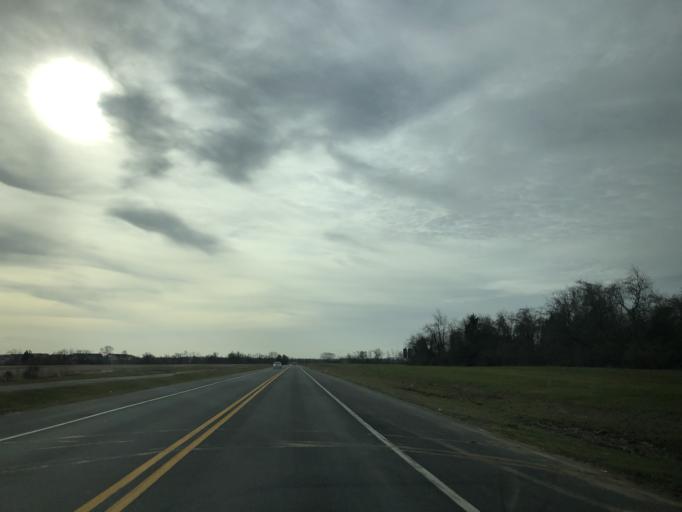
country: US
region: Delaware
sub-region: New Castle County
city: Middletown
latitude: 39.5206
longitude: -75.6793
